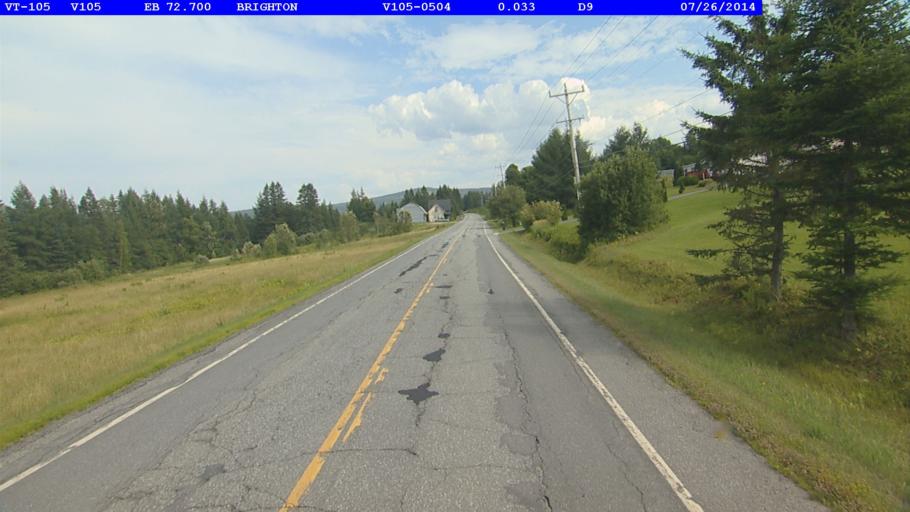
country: US
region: Vermont
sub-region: Caledonia County
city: Lyndonville
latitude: 44.8137
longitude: -71.9457
